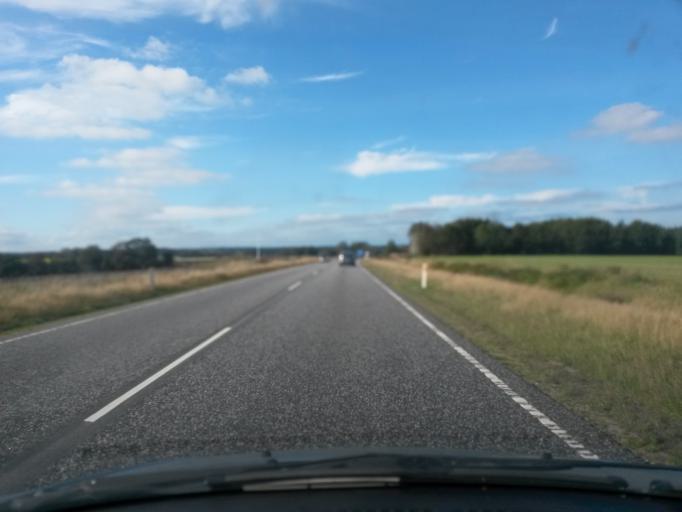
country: DK
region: Central Jutland
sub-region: Herning Kommune
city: Avlum
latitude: 56.2296
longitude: 8.8186
